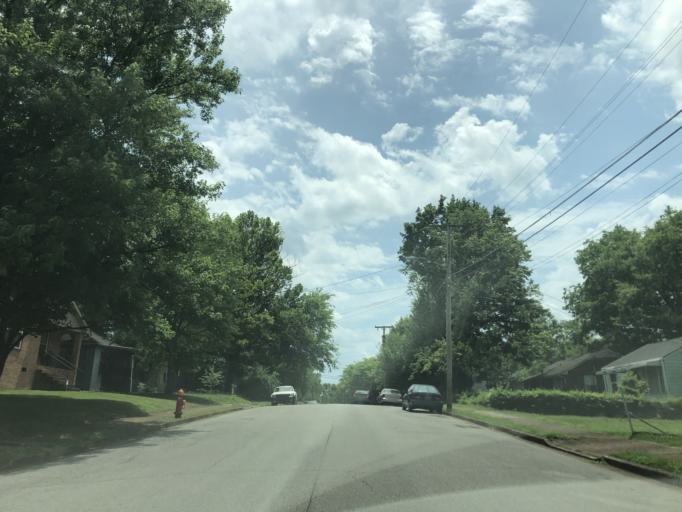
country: US
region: Tennessee
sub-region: Davidson County
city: Nashville
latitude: 36.1835
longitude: -86.7573
